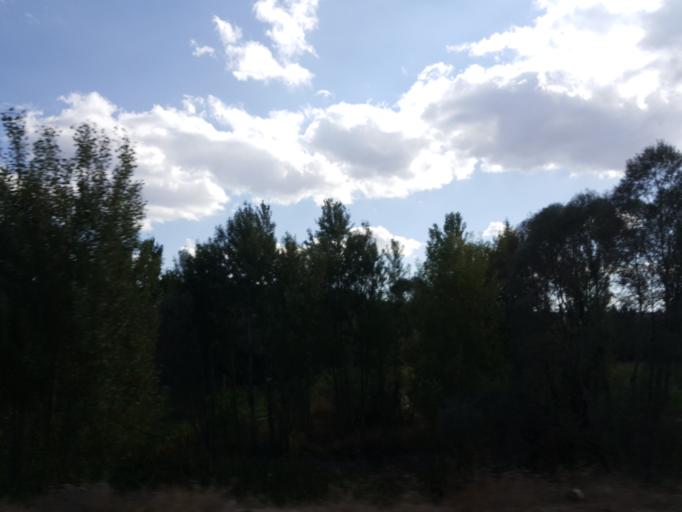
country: TR
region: Tokat
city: Sulusaray
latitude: 39.9756
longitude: 36.0475
